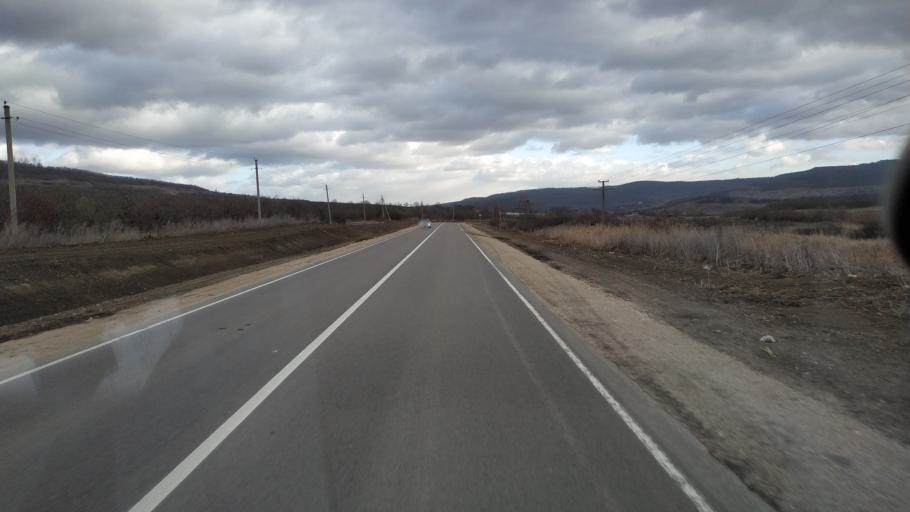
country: MD
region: Calarasi
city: Calarasi
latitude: 47.2659
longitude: 28.2307
